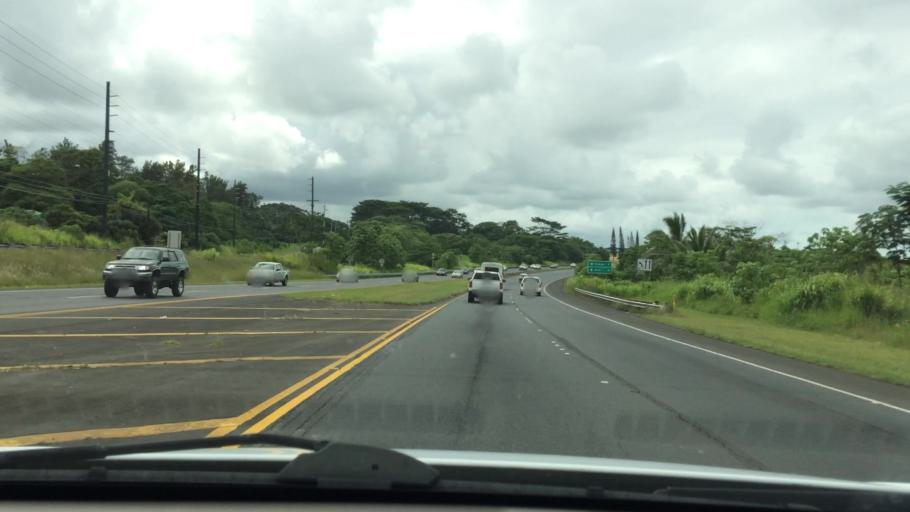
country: US
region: Hawaii
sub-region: Hawaii County
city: Kea'au
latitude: 19.6066
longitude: -155.0279
